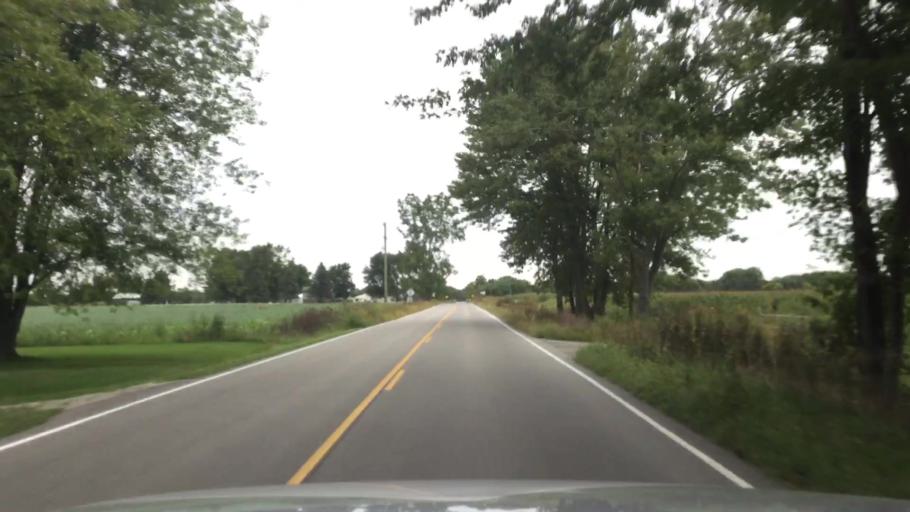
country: US
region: Michigan
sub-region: Washtenaw County
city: Milan
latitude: 42.0854
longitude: -83.7350
